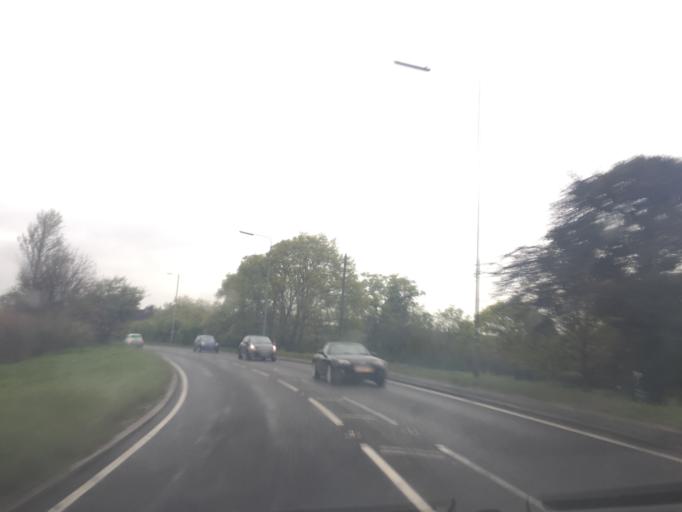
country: GB
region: England
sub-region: Essex
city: Epping
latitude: 51.7182
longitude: 0.1293
